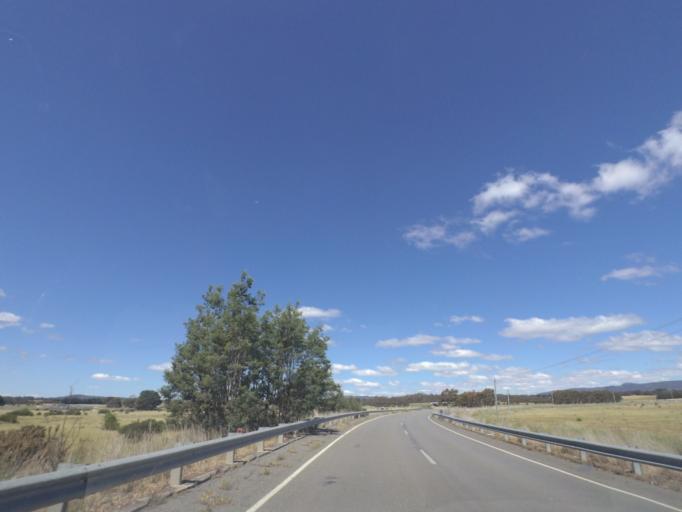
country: AU
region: Victoria
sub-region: Mount Alexander
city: Castlemaine
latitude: -37.2920
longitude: 144.4950
